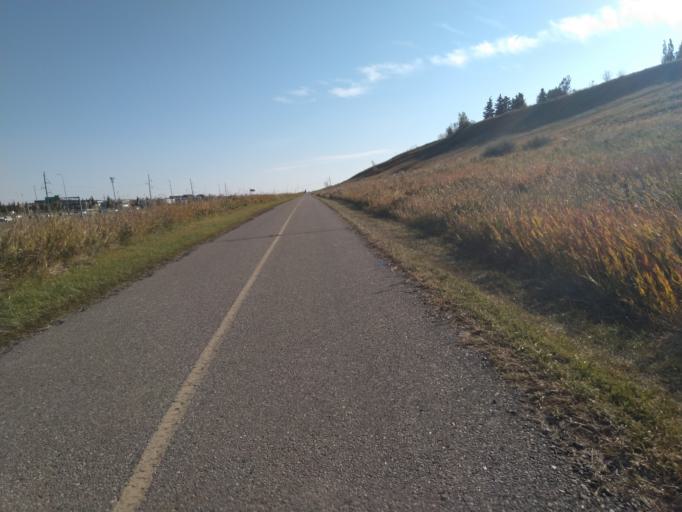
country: CA
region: Alberta
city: Calgary
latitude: 51.1224
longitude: -114.0482
